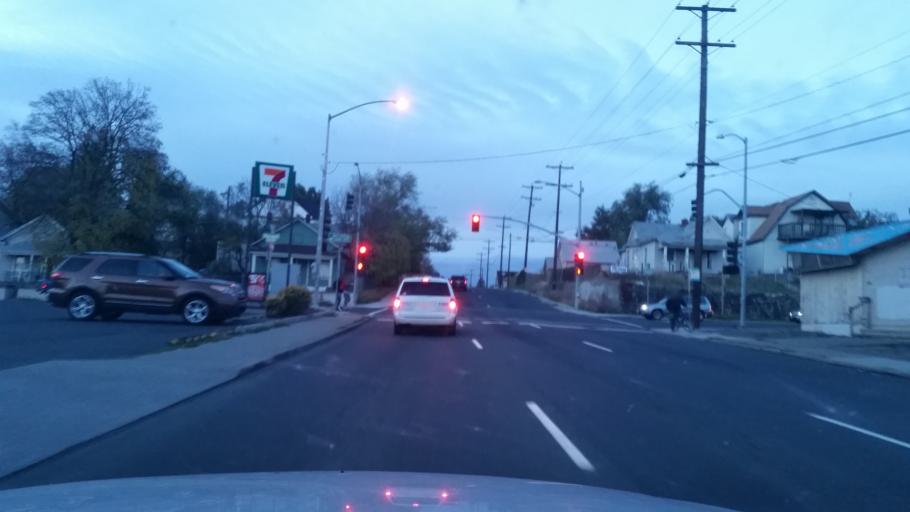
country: US
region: Washington
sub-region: Spokane County
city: Spokane
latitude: 47.6704
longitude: -117.4356
